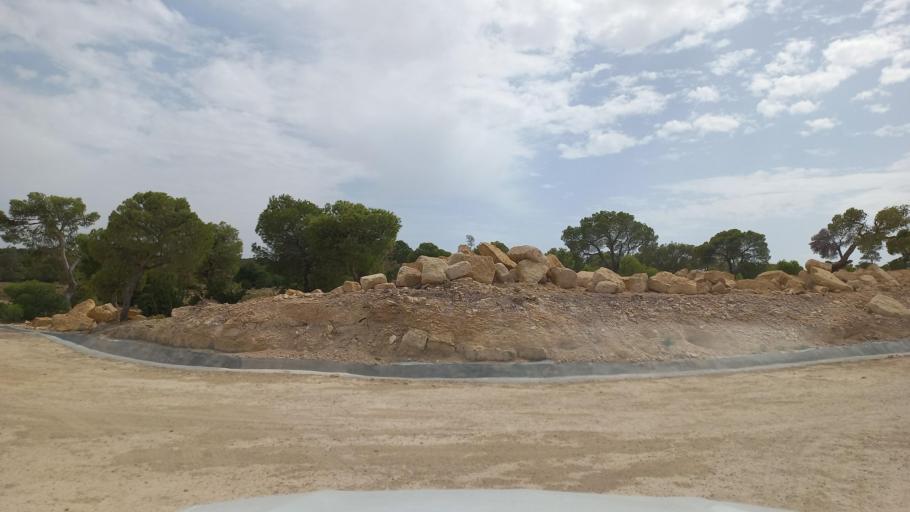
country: TN
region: Al Qasrayn
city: Kasserine
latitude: 35.3843
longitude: 8.8673
